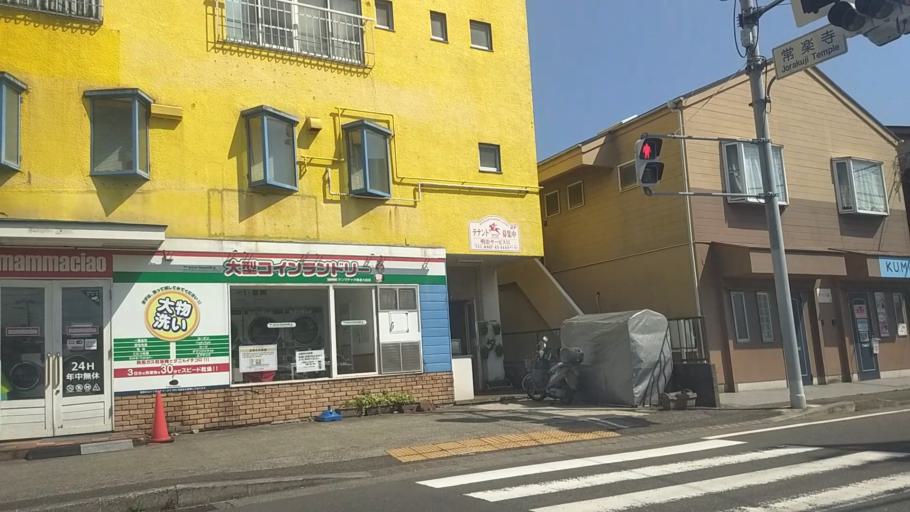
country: JP
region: Kanagawa
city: Kamakura
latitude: 35.3465
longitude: 139.5416
